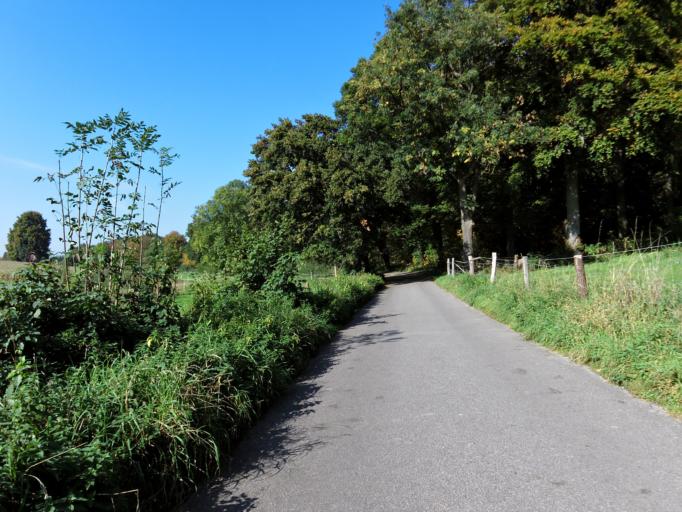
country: DE
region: North Rhine-Westphalia
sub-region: Regierungsbezirk Koln
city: Ubach-Palenberg
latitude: 50.8988
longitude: 6.1232
